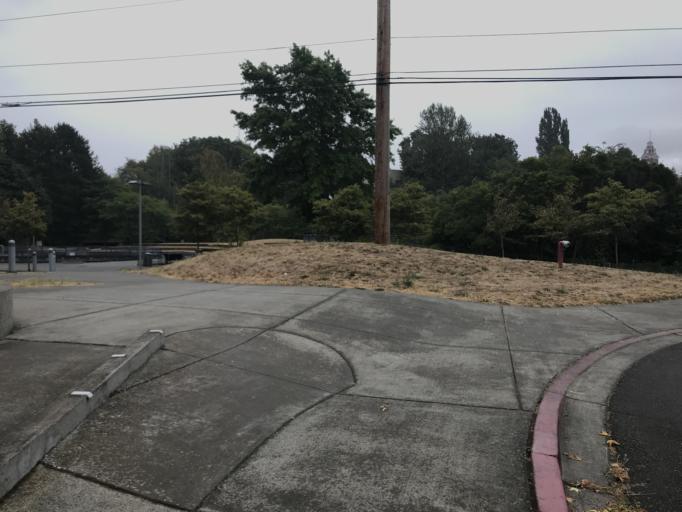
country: US
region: Washington
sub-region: Whatcom County
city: Bellingham
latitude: 48.7552
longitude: -122.4837
